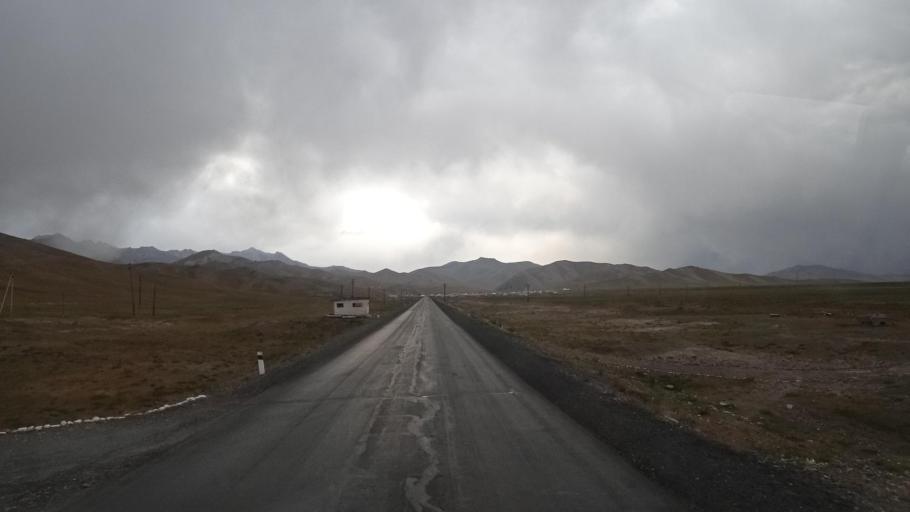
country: KG
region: Osh
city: Gul'cha
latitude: 39.7131
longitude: 73.2373
